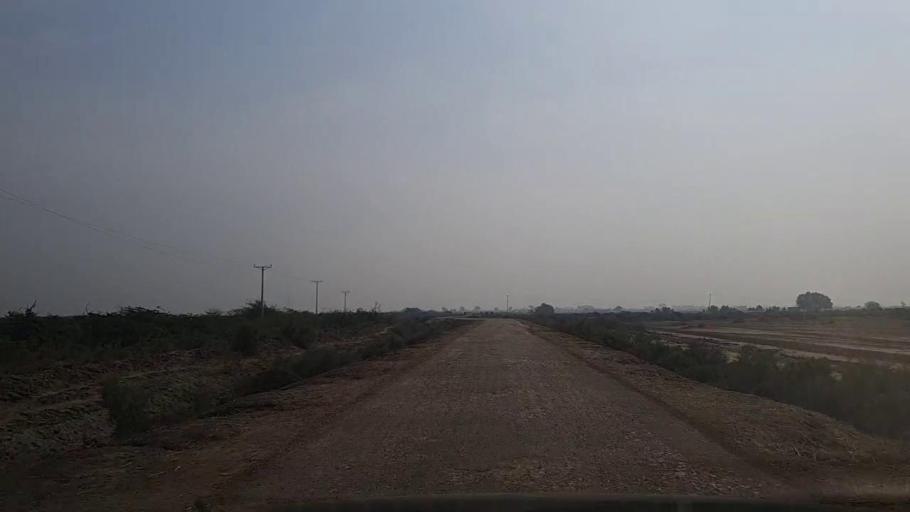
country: PK
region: Sindh
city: Mirpur Sakro
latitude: 24.3866
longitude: 67.7527
